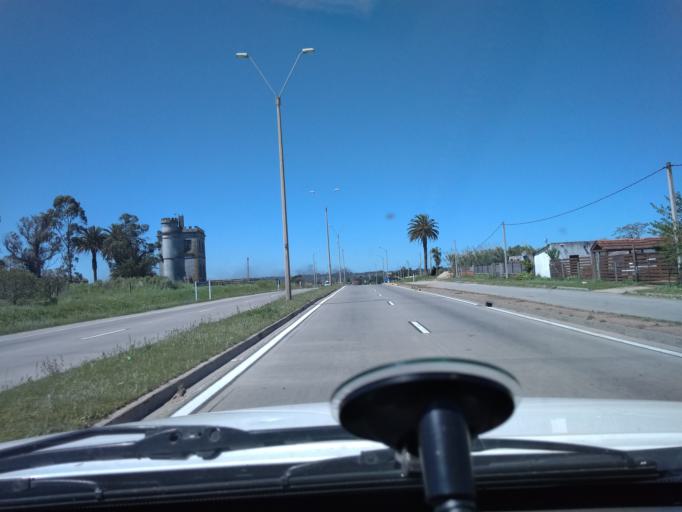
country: UY
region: Canelones
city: Toledo
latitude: -34.7948
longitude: -56.1258
